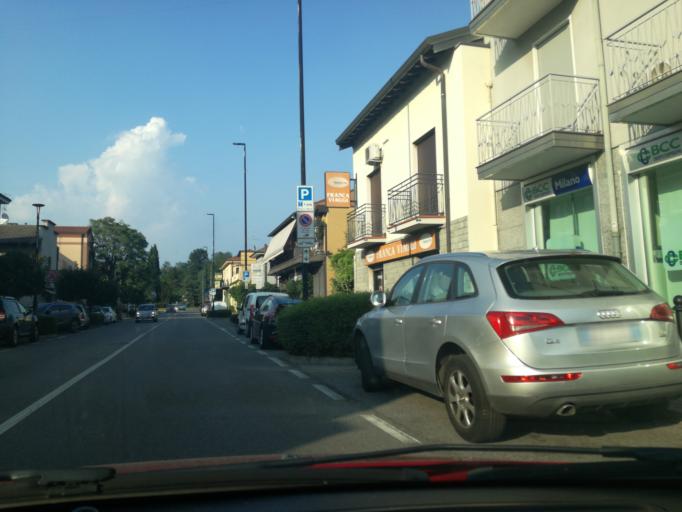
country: IT
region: Lombardy
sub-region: Provincia di Monza e Brianza
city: Usmate-Velate
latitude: 45.6526
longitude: 9.3653
